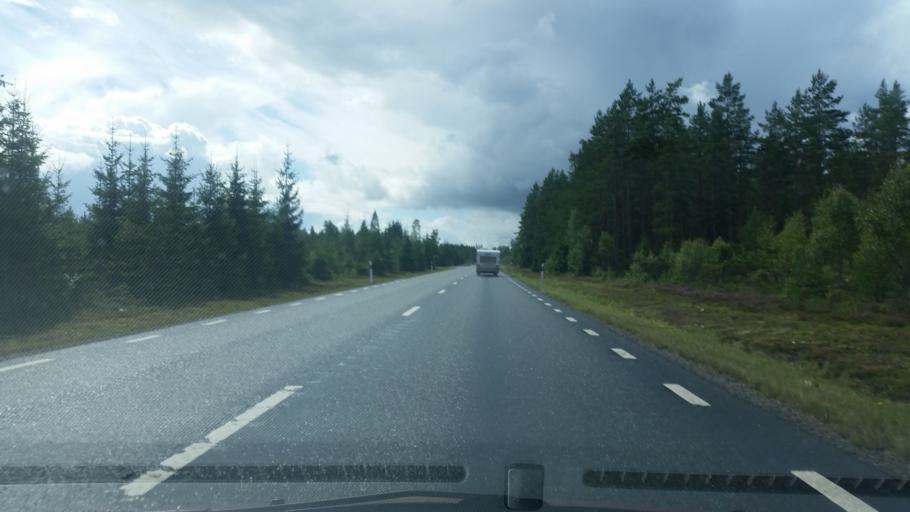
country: SE
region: Joenkoeping
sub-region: Gislaveds Kommun
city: Gislaved
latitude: 57.3691
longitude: 13.5732
